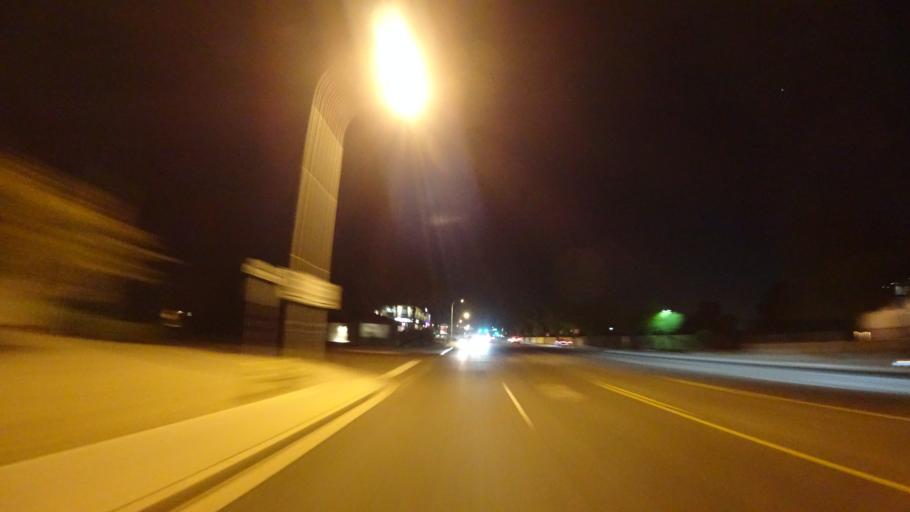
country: US
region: Arizona
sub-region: Maricopa County
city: Paradise Valley
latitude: 33.4948
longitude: -111.9812
